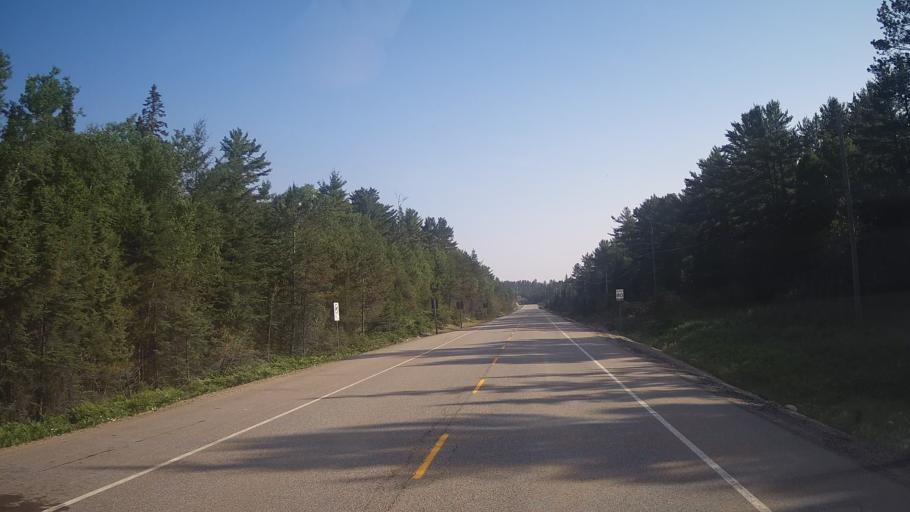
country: CA
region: Ontario
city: Rayside-Balfour
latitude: 46.7510
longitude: -81.6001
